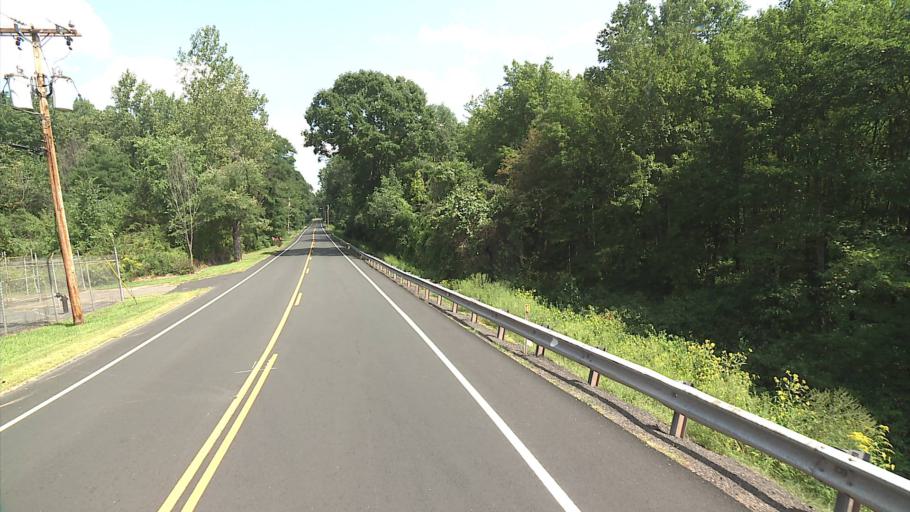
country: US
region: Connecticut
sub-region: Hartford County
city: Broad Brook
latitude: 41.9084
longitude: -72.5702
